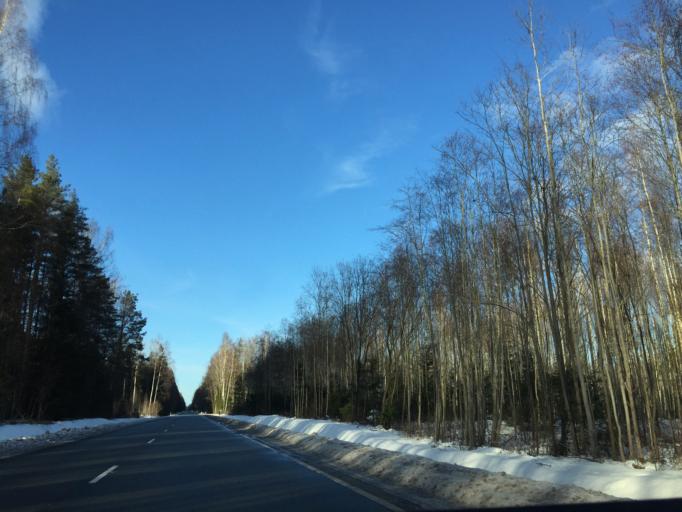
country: LV
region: Lielvarde
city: Lielvarde
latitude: 56.6632
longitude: 24.8688
